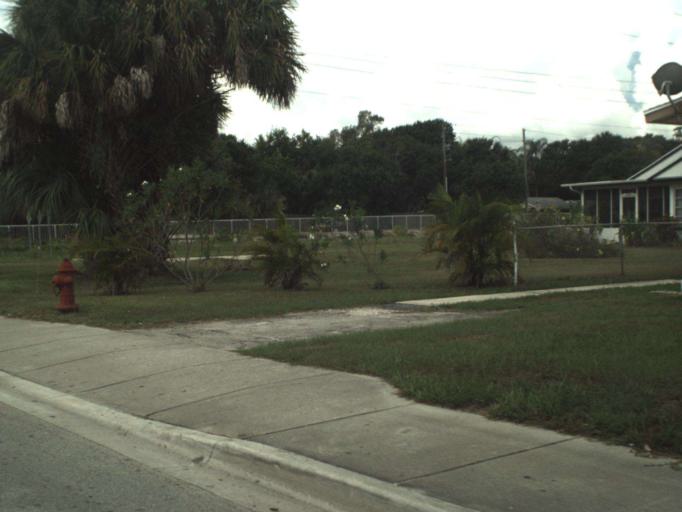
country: US
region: Florida
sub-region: Saint Lucie County
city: Fort Pierce South
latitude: 27.4192
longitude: -80.3502
